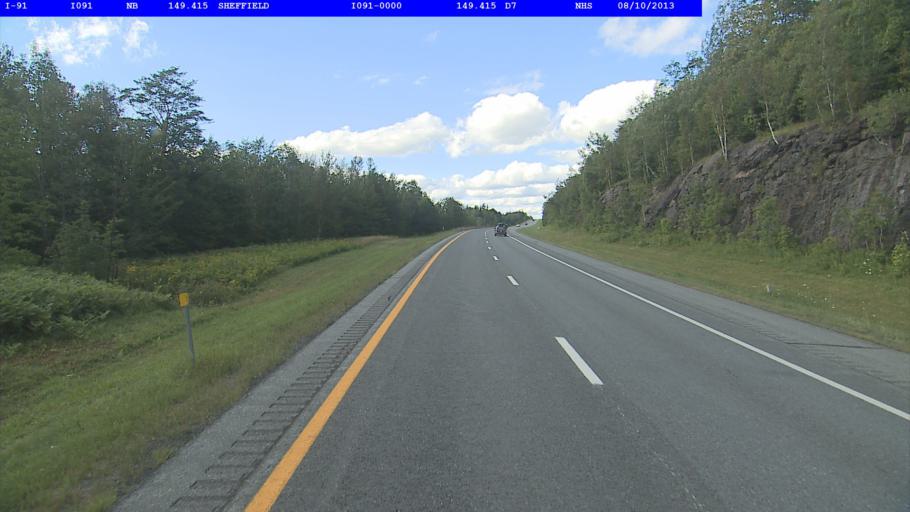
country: US
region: Vermont
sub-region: Caledonia County
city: Lyndonville
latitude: 44.6561
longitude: -72.1338
